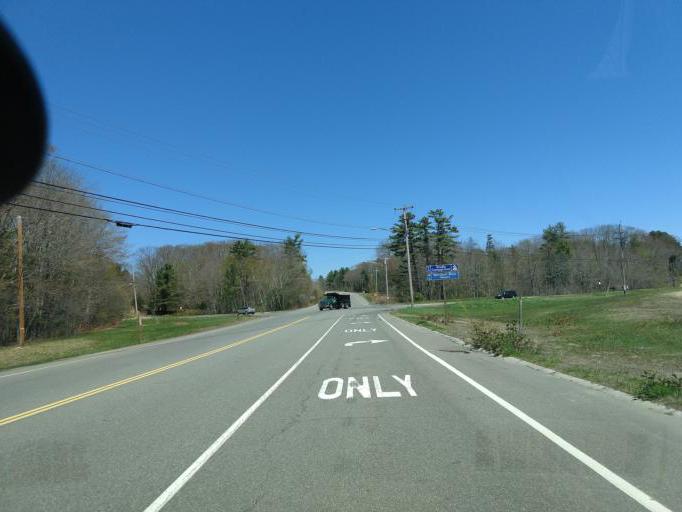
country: US
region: Maine
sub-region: York County
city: Wells Beach Station
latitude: 43.3440
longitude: -70.5616
